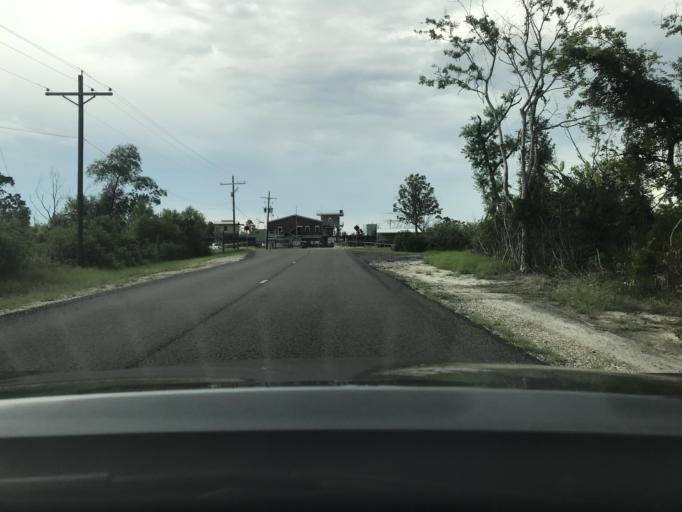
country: US
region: Louisiana
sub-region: Calcasieu Parish
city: Westlake
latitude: 30.2556
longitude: -93.2186
